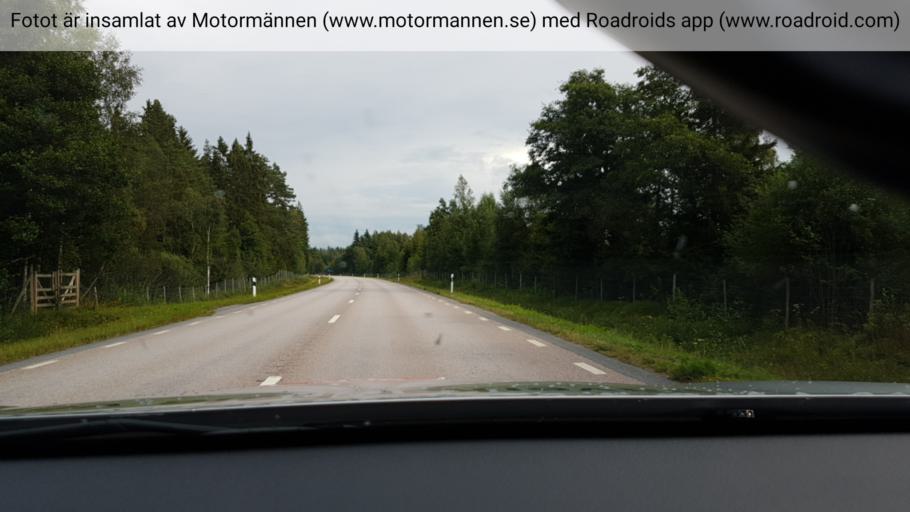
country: SE
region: Uppsala
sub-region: Osthammars Kommun
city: Osterbybruk
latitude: 60.3994
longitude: 17.8867
